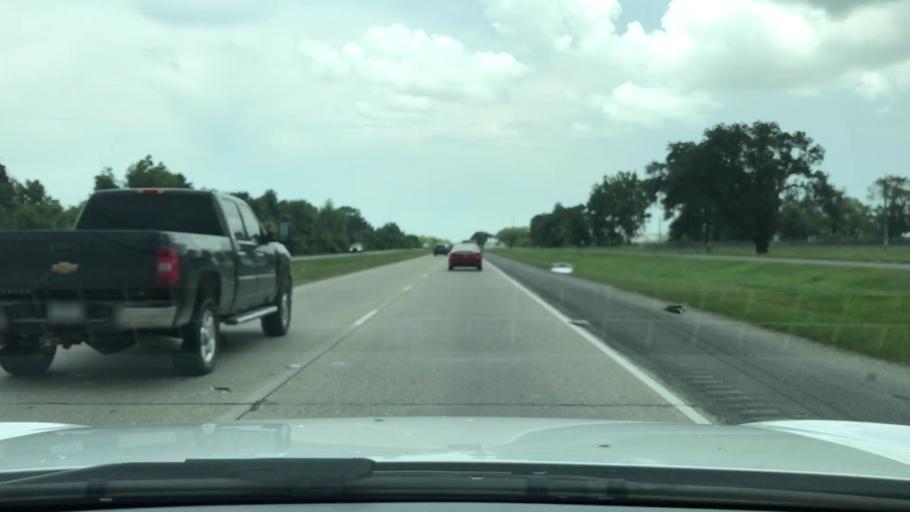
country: US
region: Louisiana
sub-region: Iberville Parish
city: Plaquemine
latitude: 30.3163
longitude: -91.2497
